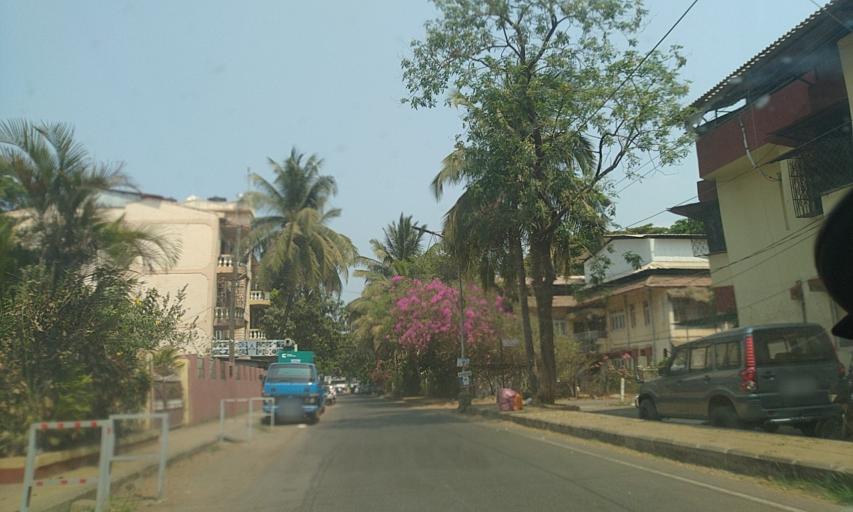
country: IN
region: Goa
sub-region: North Goa
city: Panaji
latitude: 15.4865
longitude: 73.8114
